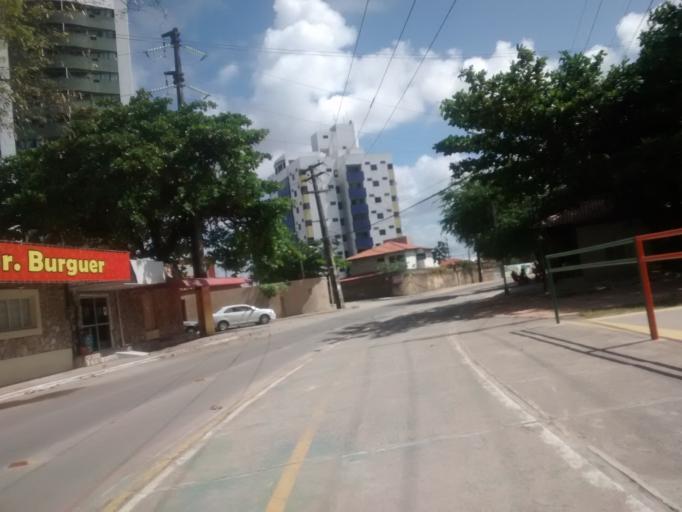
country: BR
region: Pernambuco
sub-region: Recife
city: Recife
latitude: -8.0959
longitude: -34.9136
